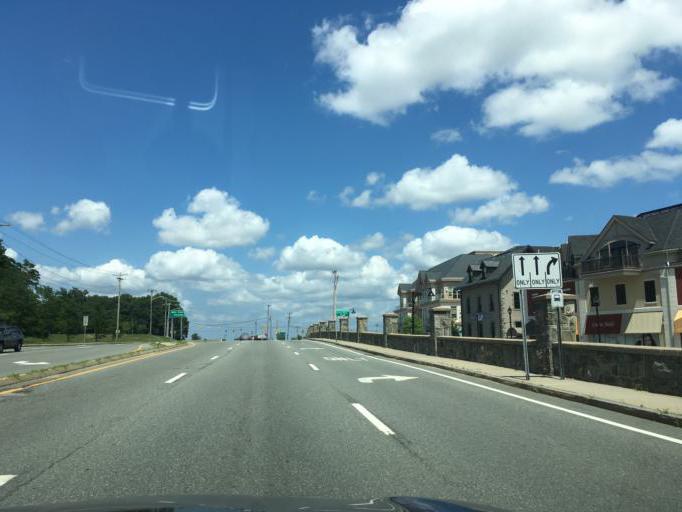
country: US
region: Rhode Island
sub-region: Providence County
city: Cranston
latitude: 41.7566
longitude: -71.4615
